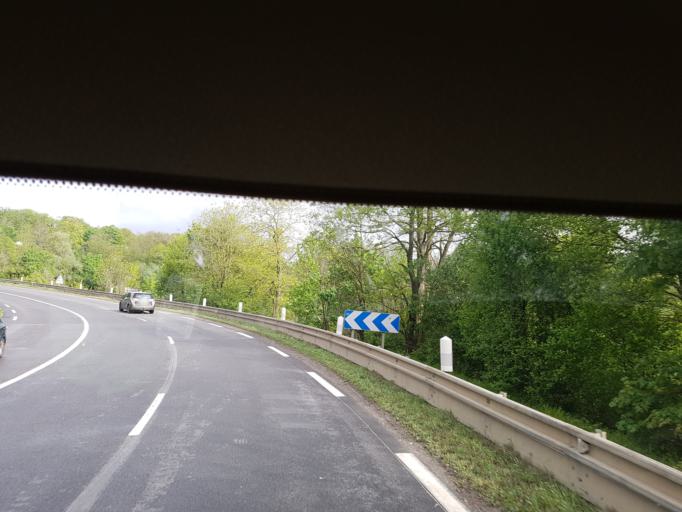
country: FR
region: Picardie
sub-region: Departement de l'Aisne
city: Cuffies
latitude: 49.4054
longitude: 3.3378
